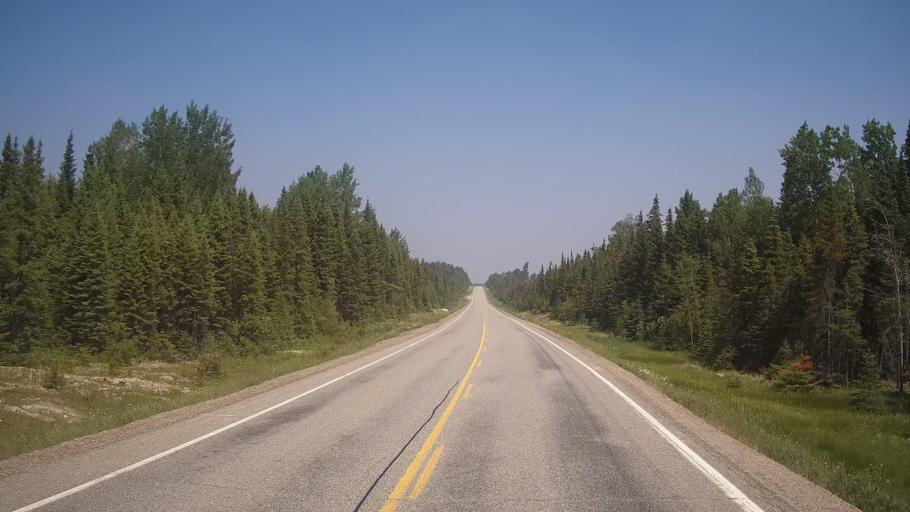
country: CA
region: Ontario
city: Timmins
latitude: 48.1741
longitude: -81.5821
